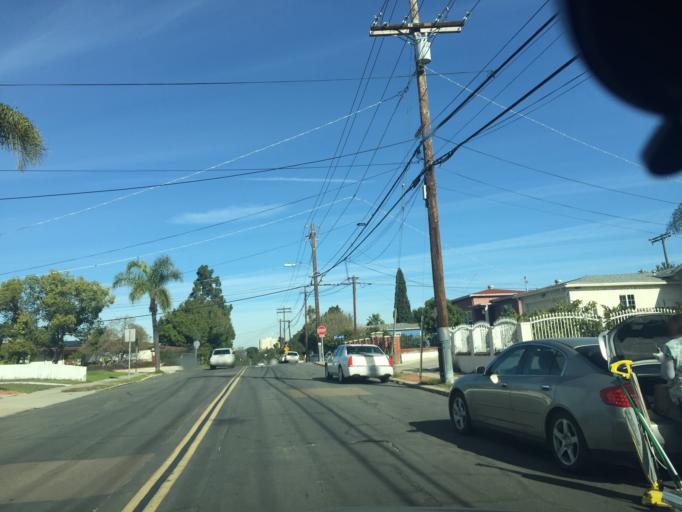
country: US
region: California
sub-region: San Diego County
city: Lemon Grove
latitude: 32.7629
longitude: -117.0793
